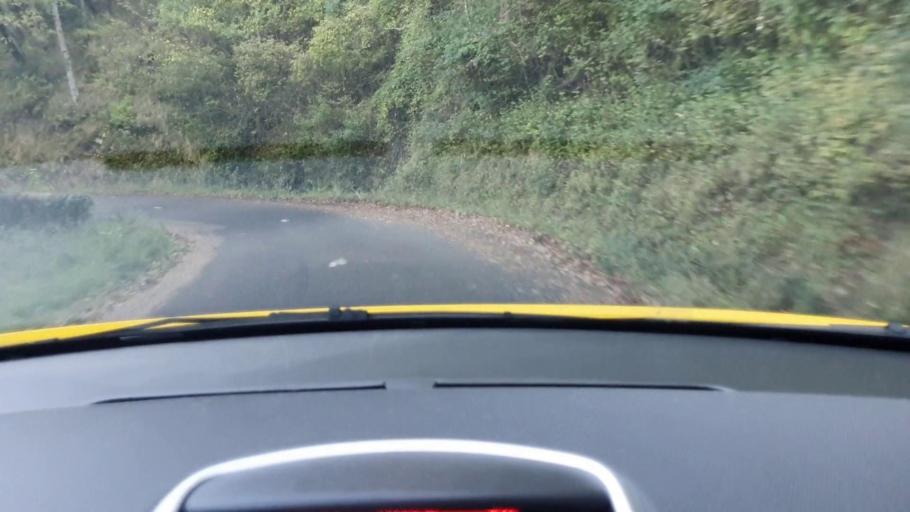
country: FR
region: Languedoc-Roussillon
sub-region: Departement du Gard
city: Sumene
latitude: 43.9718
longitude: 3.7813
